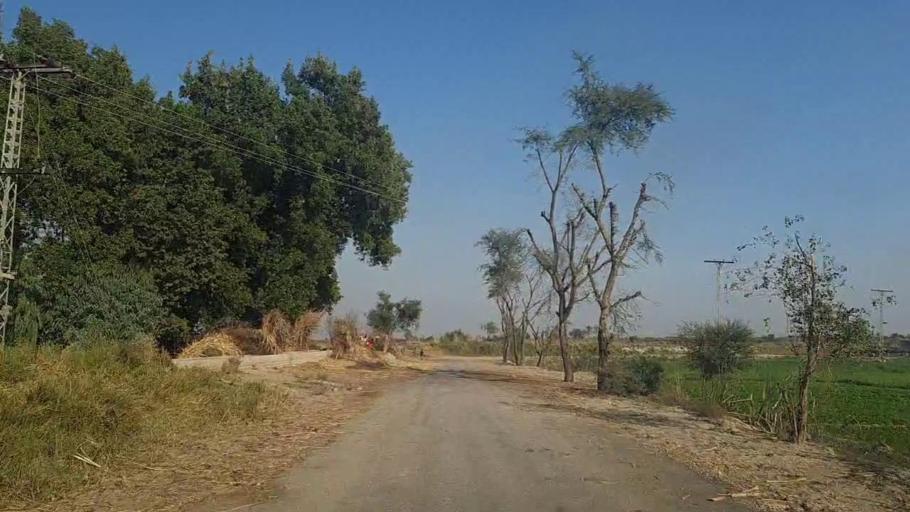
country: PK
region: Sindh
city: Jam Sahib
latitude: 26.3352
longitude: 68.7610
